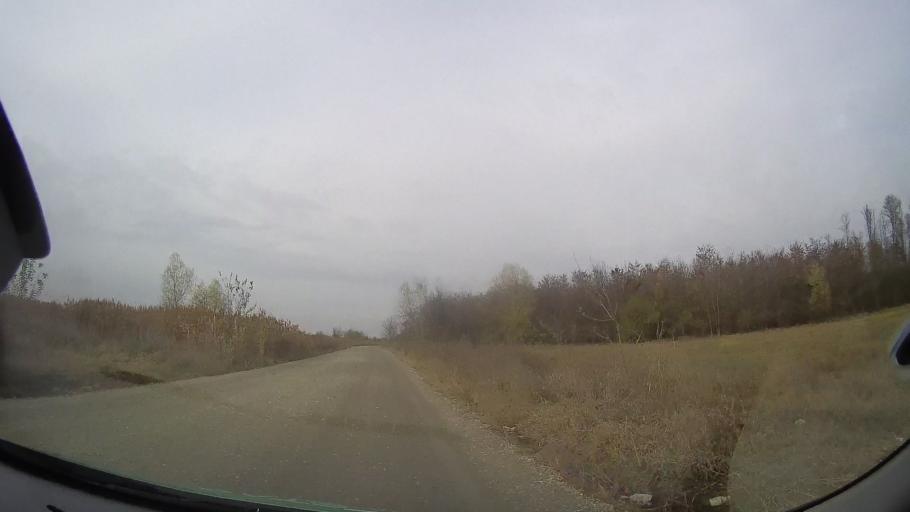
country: RO
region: Ialomita
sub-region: Comuna Fierbinti-Targ
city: Fierbinti-Targ
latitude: 44.6780
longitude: 26.3483
